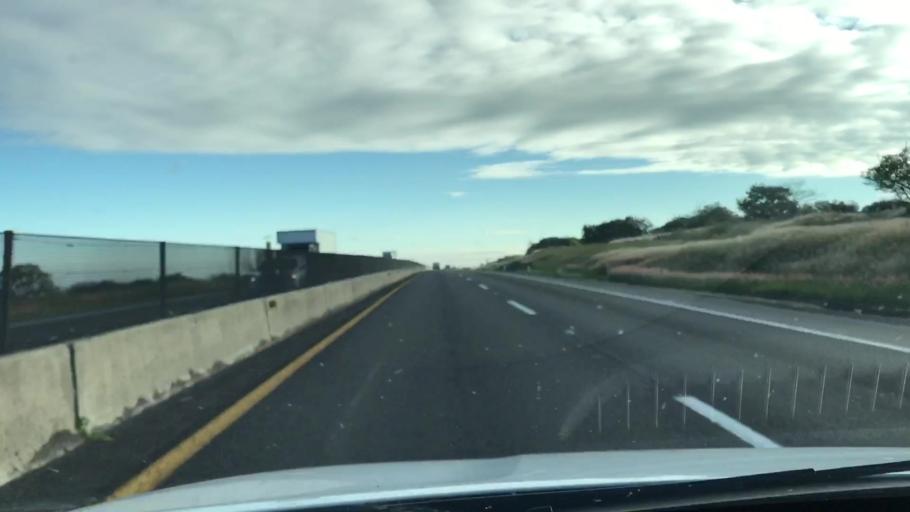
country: MX
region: Jalisco
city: Valle de Guadalupe
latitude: 21.0581
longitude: -102.5215
